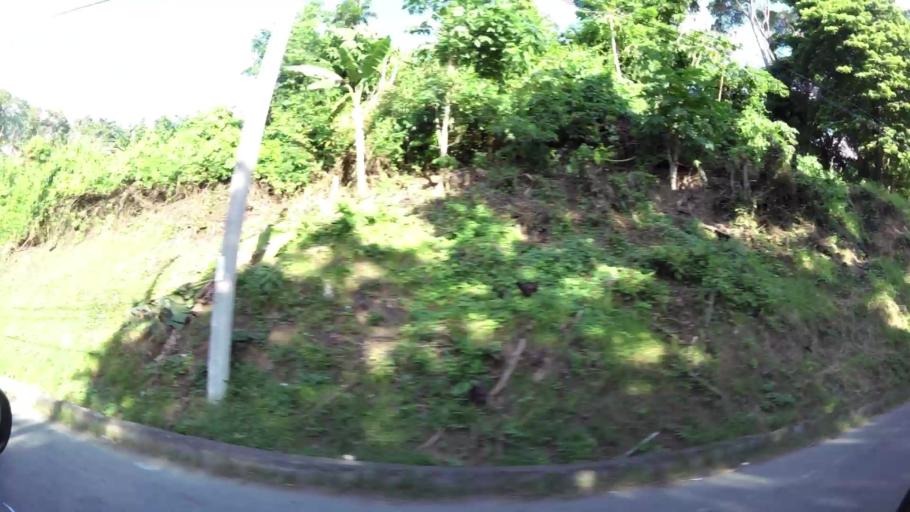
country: TT
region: Tobago
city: Scarborough
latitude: 11.1927
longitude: -60.6835
